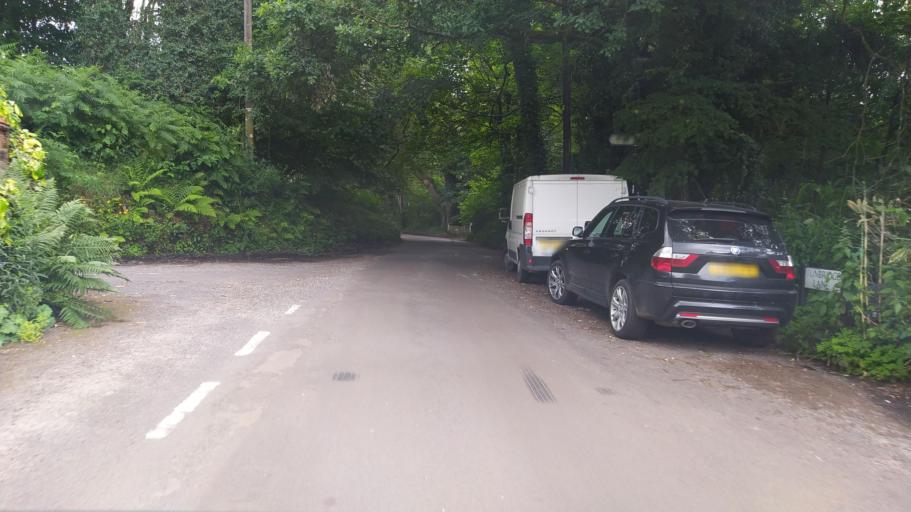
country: GB
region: England
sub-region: Hampshire
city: Liphook
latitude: 51.0896
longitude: -0.8036
